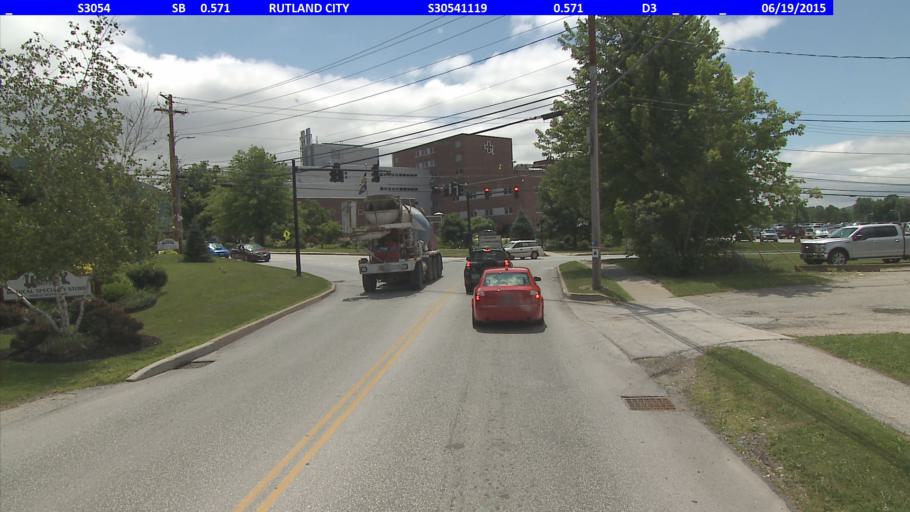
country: US
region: Vermont
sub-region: Rutland County
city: Rutland
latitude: 43.5997
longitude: -72.9556
